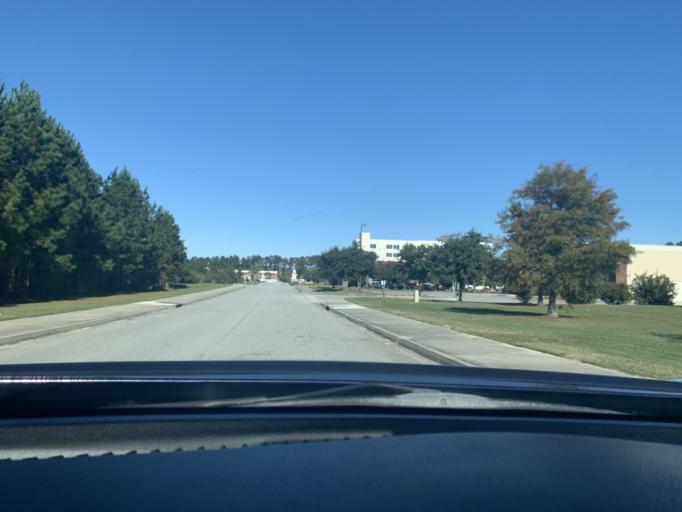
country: US
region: Georgia
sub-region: Chatham County
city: Pooler
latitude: 32.1433
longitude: -81.2489
